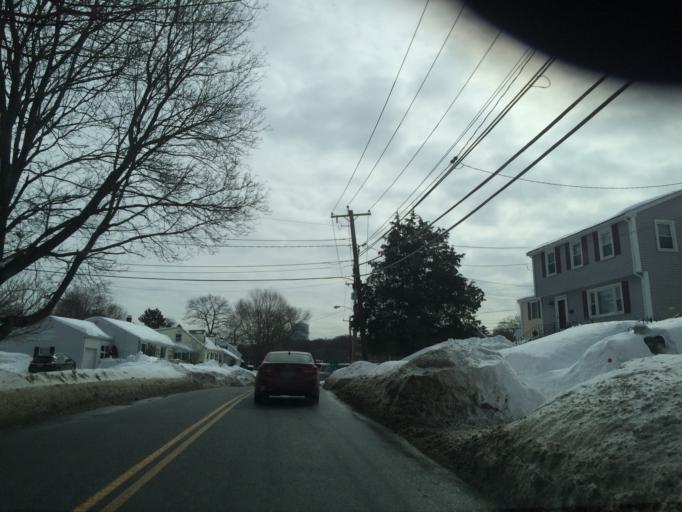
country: US
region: Massachusetts
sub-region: Middlesex County
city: Waltham
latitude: 42.3751
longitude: -71.2635
